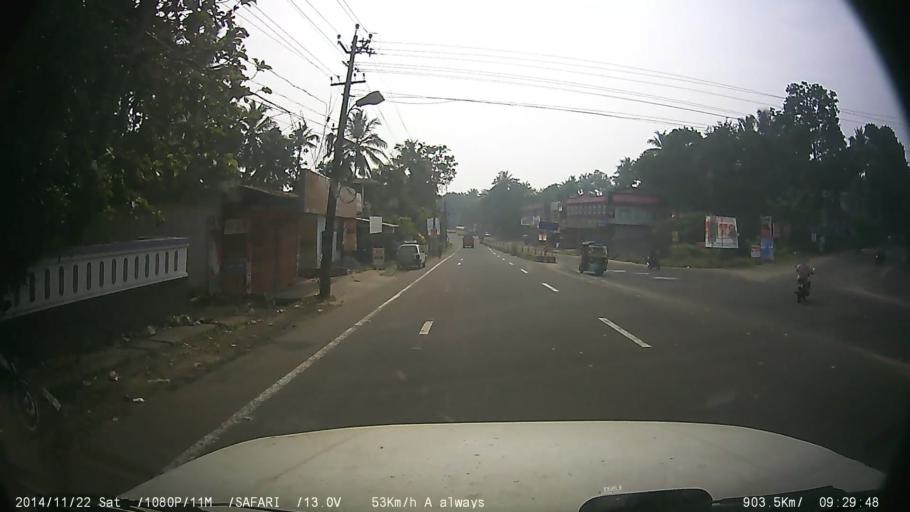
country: IN
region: Kerala
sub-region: Ernakulam
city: Angamali
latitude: 10.1863
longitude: 76.3969
